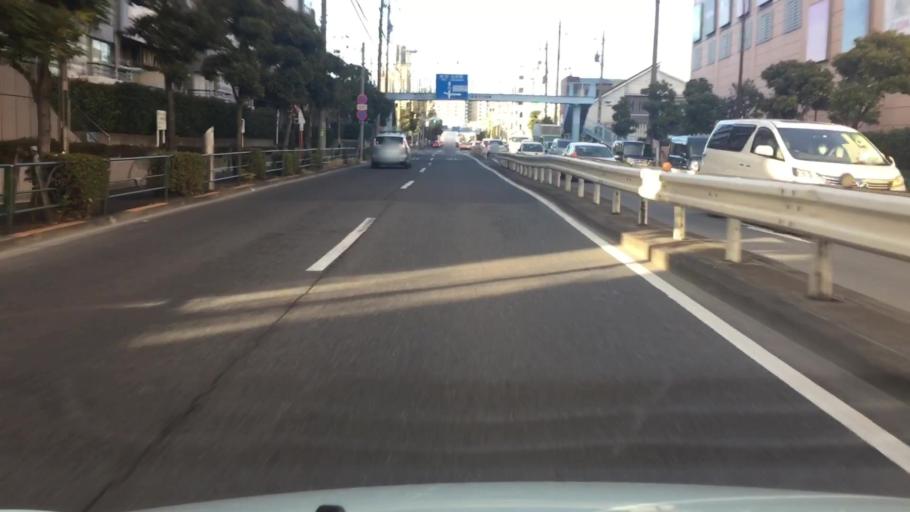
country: JP
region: Saitama
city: Soka
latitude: 35.7744
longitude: 139.7846
